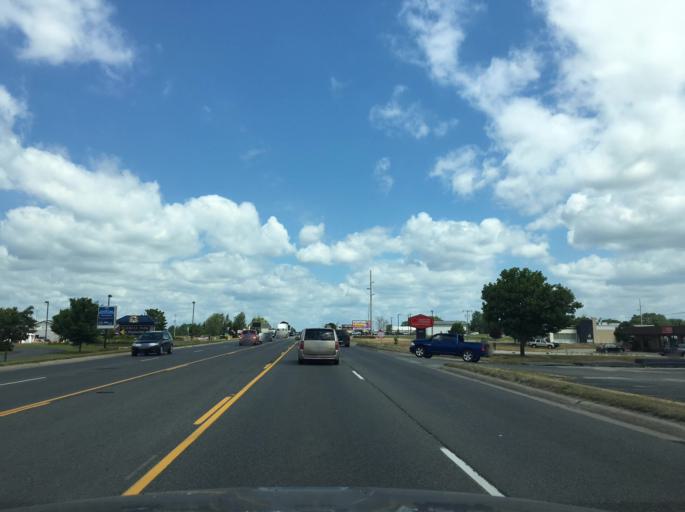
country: US
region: Michigan
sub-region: Grand Traverse County
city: Traverse City
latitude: 44.6771
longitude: -85.6563
